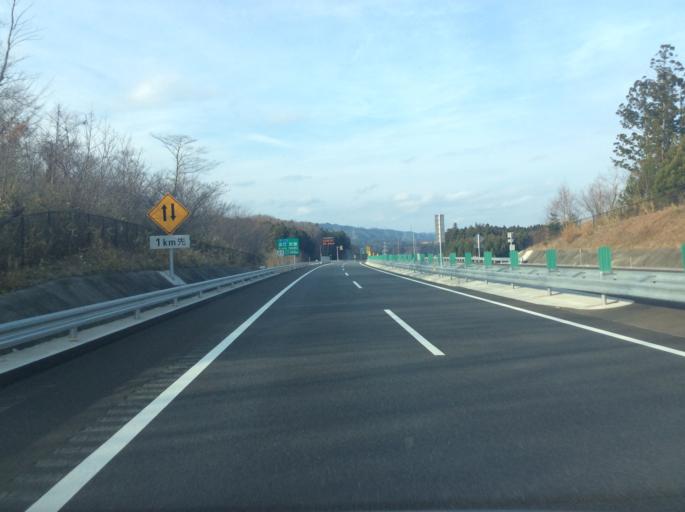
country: JP
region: Fukushima
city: Namie
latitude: 37.4938
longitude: 140.9453
